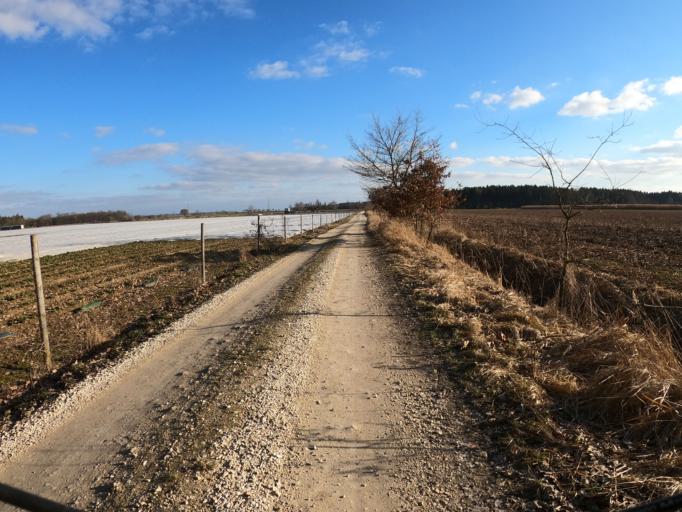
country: DE
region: Bavaria
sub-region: Swabia
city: Bubesheim
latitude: 48.4192
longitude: 10.2314
